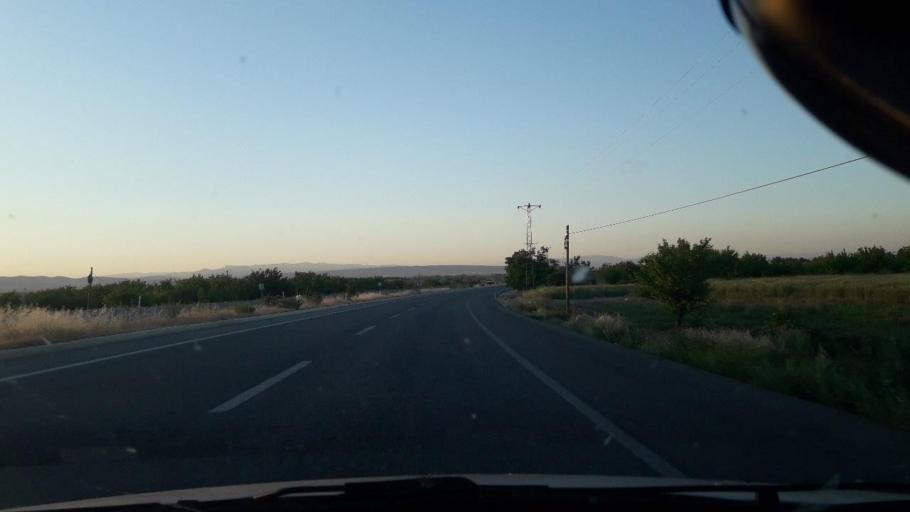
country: TR
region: Malatya
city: Yazihan
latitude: 38.4887
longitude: 38.2160
